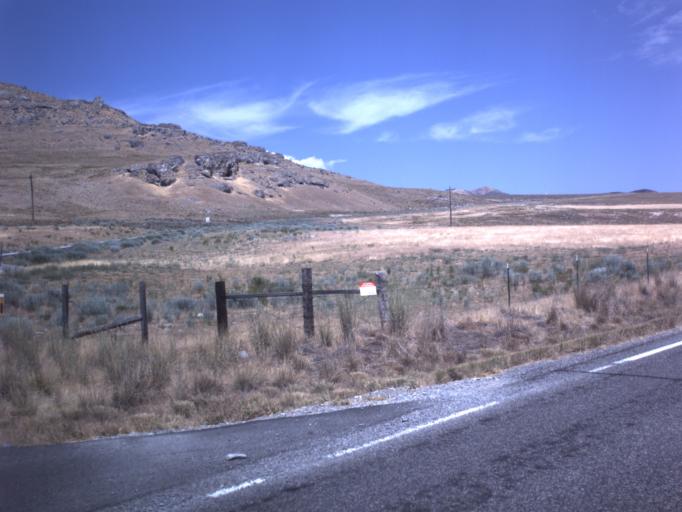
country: US
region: Utah
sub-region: Box Elder County
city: Tremonton
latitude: 41.6176
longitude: -112.3665
